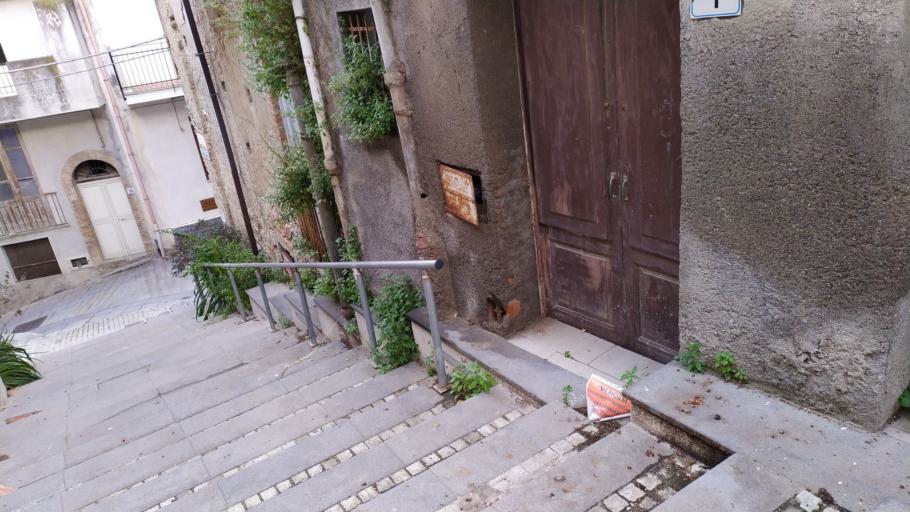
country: IT
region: Sicily
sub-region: Messina
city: Gualtieri Sicamino
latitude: 38.1615
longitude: 15.3146
